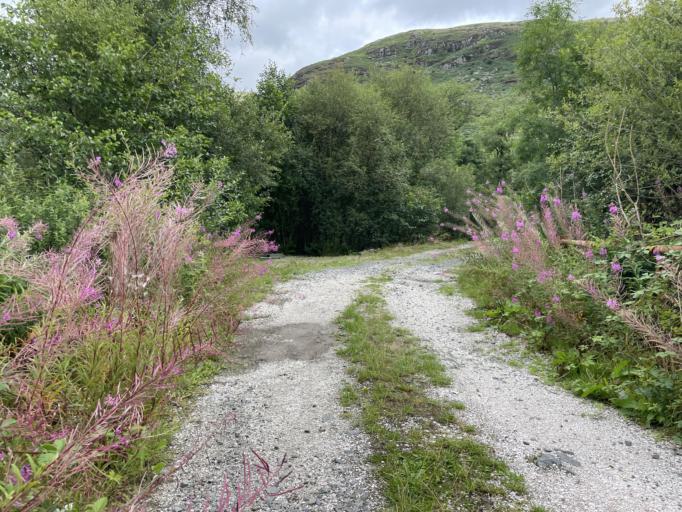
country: GB
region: Scotland
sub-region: Dumfries and Galloway
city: Newton Stewart
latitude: 55.0884
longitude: -4.4583
